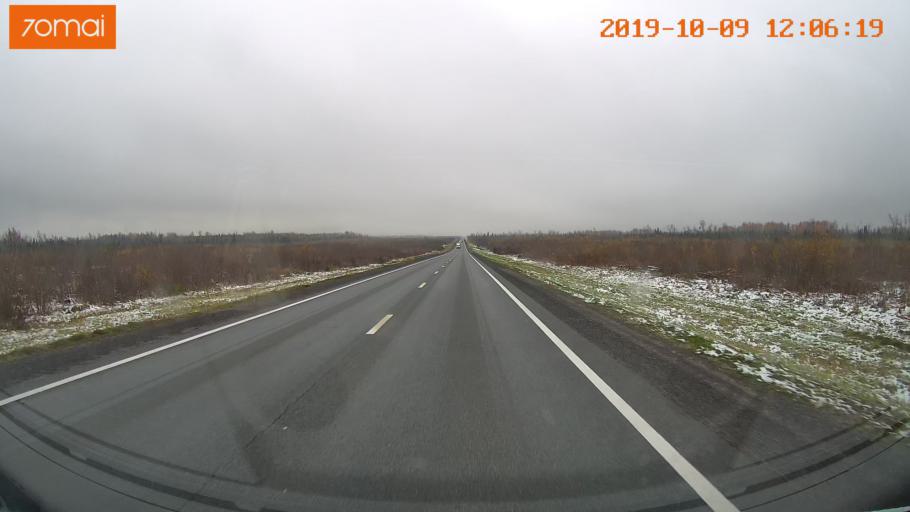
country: RU
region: Jaroslavl
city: Prechistoye
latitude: 58.6163
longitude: 40.3344
